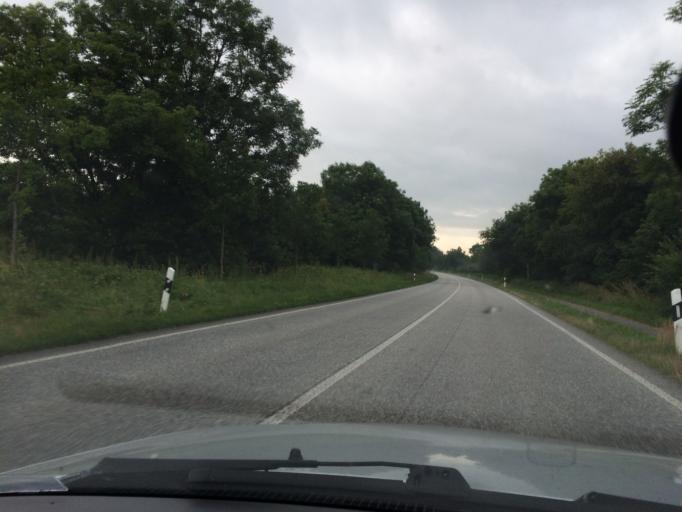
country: DE
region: Schleswig-Holstein
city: Sieverstedt
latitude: 54.6512
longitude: 9.4456
